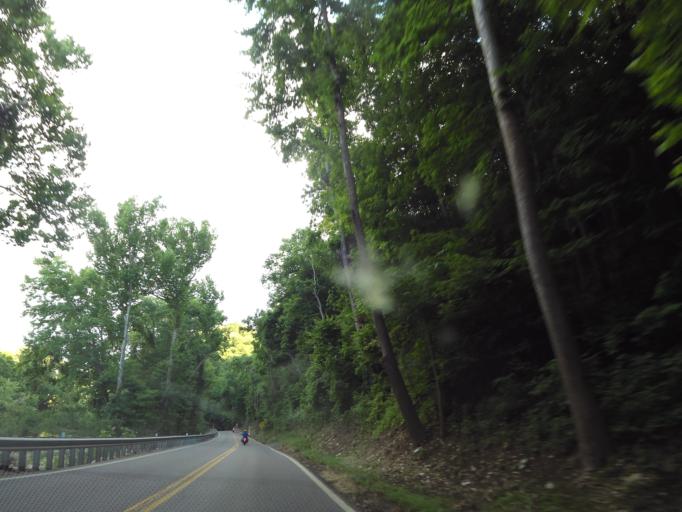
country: US
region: Missouri
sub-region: Saint Louis County
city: Eureka
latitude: 38.4562
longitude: -90.6251
